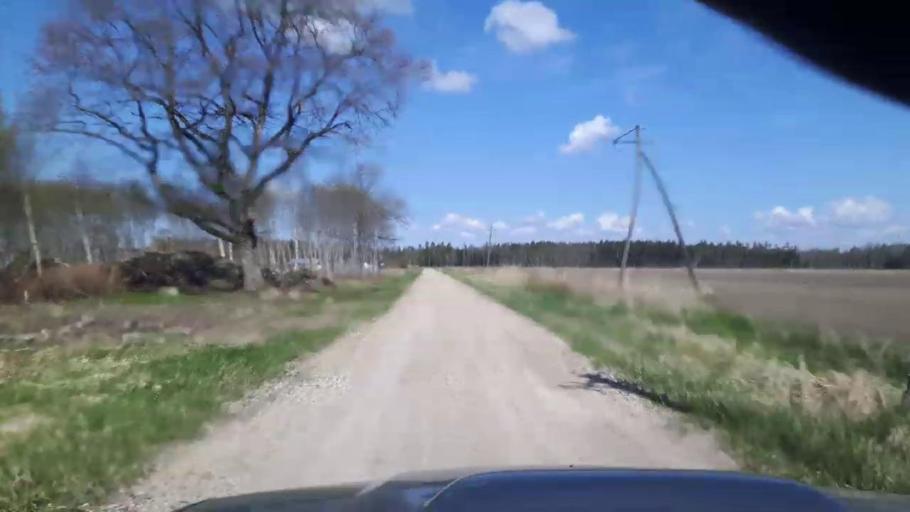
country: EE
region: Paernumaa
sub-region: Vaendra vald (alev)
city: Vandra
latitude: 58.5137
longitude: 25.0428
